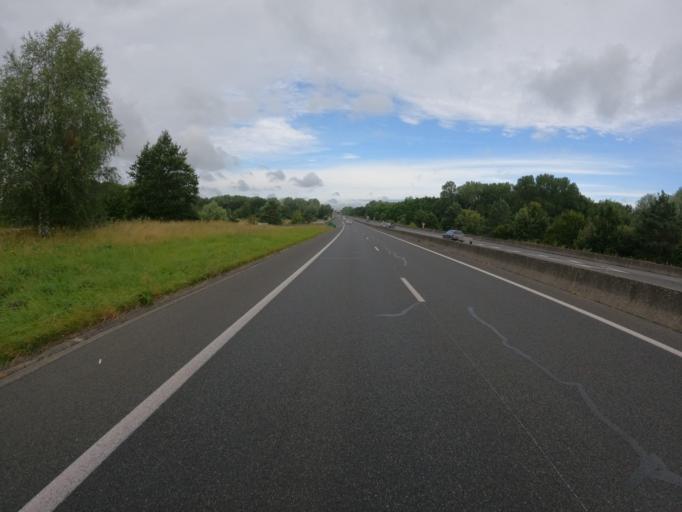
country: FR
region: Centre
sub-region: Departement d'Indre-et-Loire
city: Cinq-Mars-la-Pile
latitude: 47.3268
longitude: 0.4756
